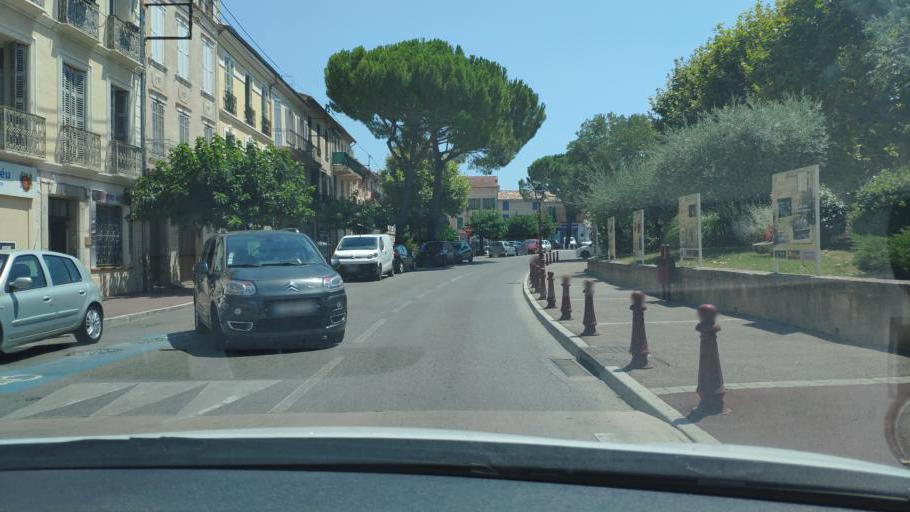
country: FR
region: Provence-Alpes-Cote d'Azur
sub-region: Departement du Var
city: Les Arcs
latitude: 43.4618
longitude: 6.4797
